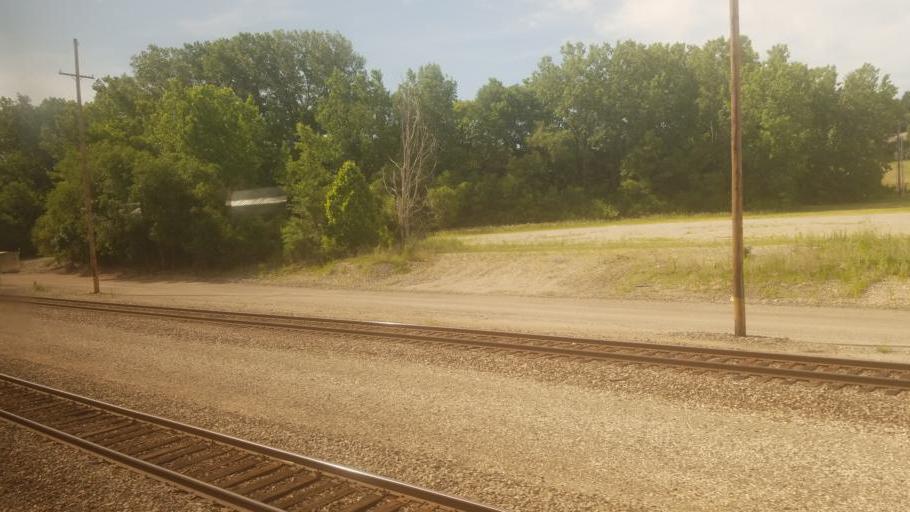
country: US
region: Kansas
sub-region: Johnson County
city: Roeland Park
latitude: 39.0749
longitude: -94.6530
